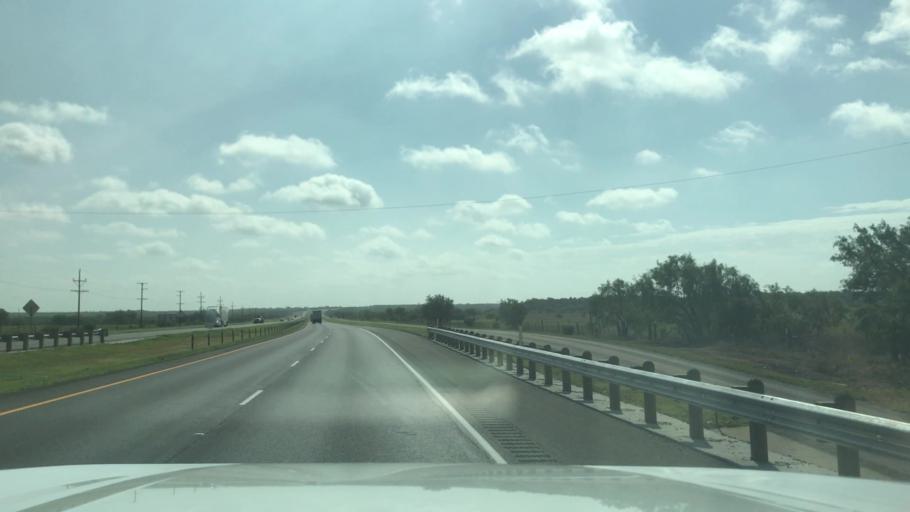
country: US
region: Texas
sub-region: Nolan County
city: Sweetwater
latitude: 32.4946
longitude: -100.2921
